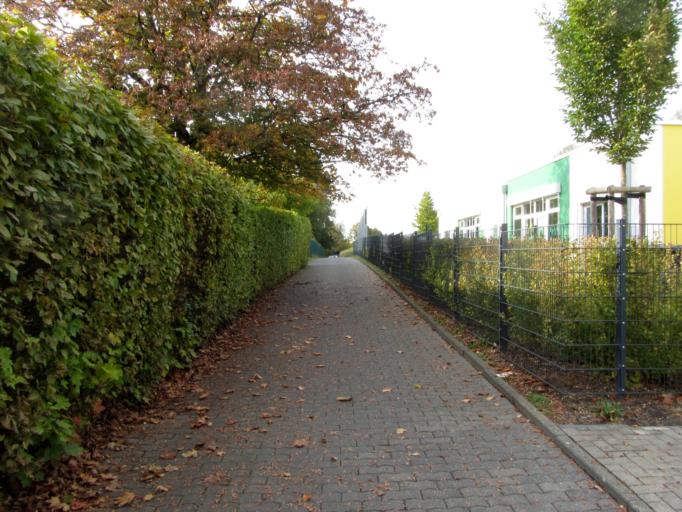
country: DE
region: North Rhine-Westphalia
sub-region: Regierungsbezirk Arnsberg
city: Siegen
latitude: 50.8851
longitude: 8.0413
